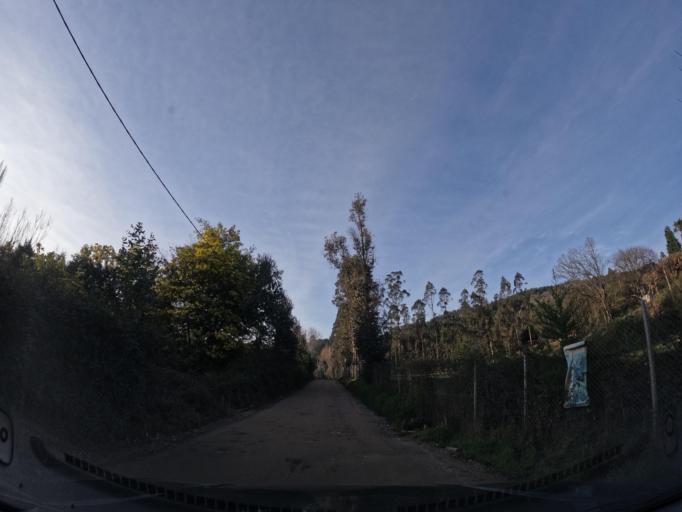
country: CL
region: Biobio
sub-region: Provincia de Concepcion
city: Concepcion
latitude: -36.8637
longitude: -72.9986
